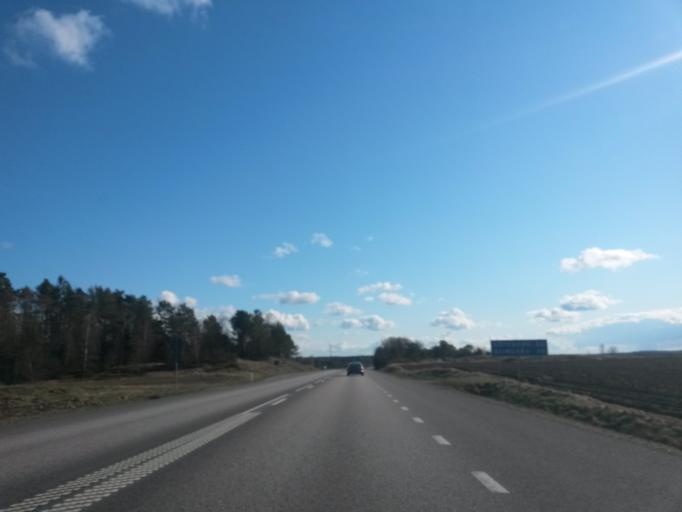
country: SE
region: Vaestra Goetaland
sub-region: Vargarda Kommun
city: Vargarda
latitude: 58.1420
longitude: 12.8632
